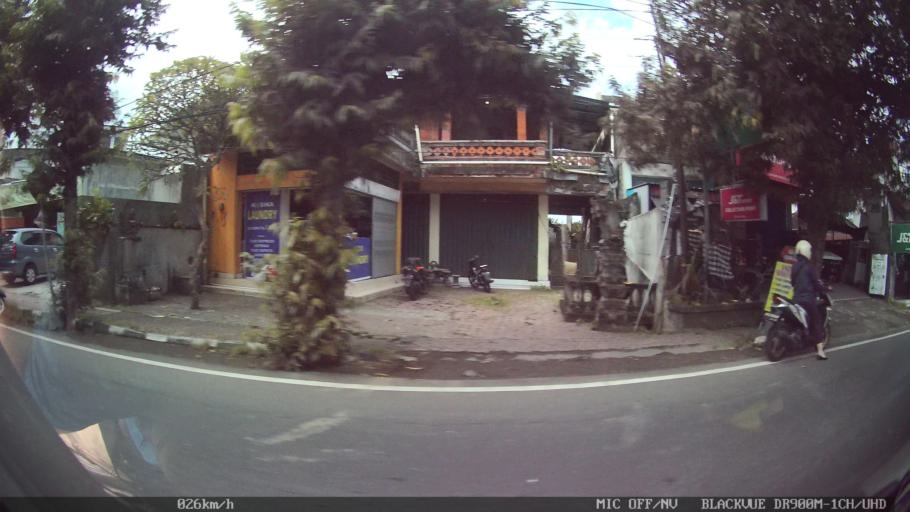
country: ID
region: Bali
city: Banjar Pesalakan
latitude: -8.5345
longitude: 115.3230
